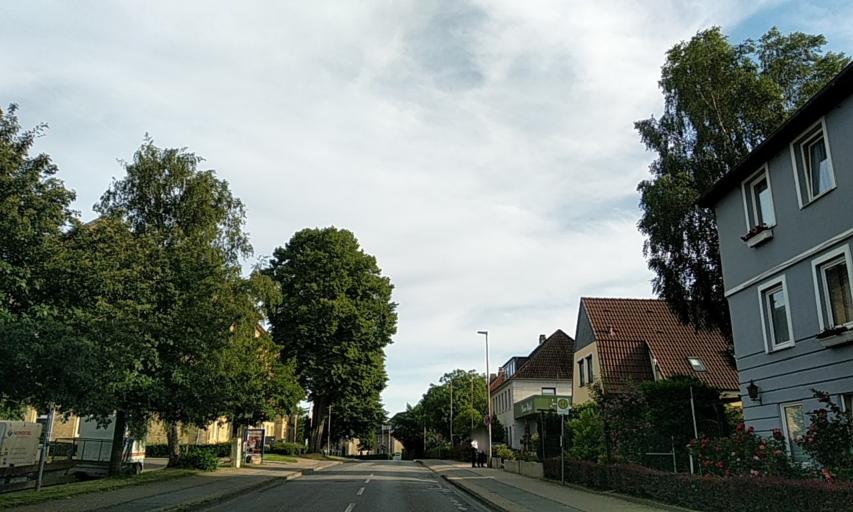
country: DE
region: Schleswig-Holstein
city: Schleswig
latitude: 54.5212
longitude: 9.5569
